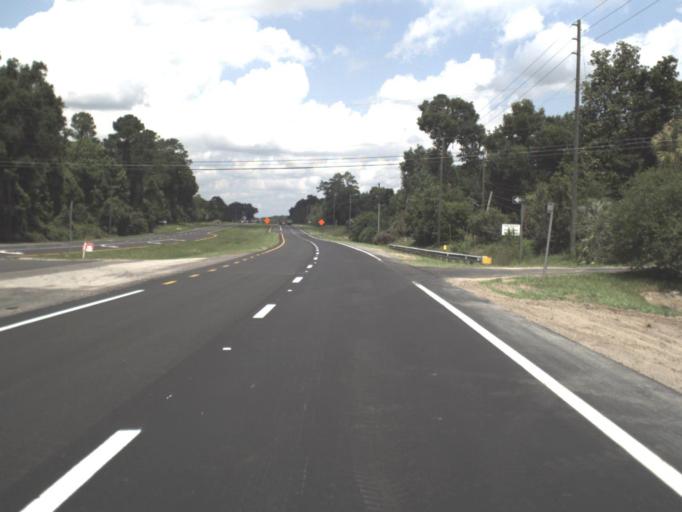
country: US
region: Florida
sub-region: Alachua County
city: Alachua
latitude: 29.7657
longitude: -82.4108
